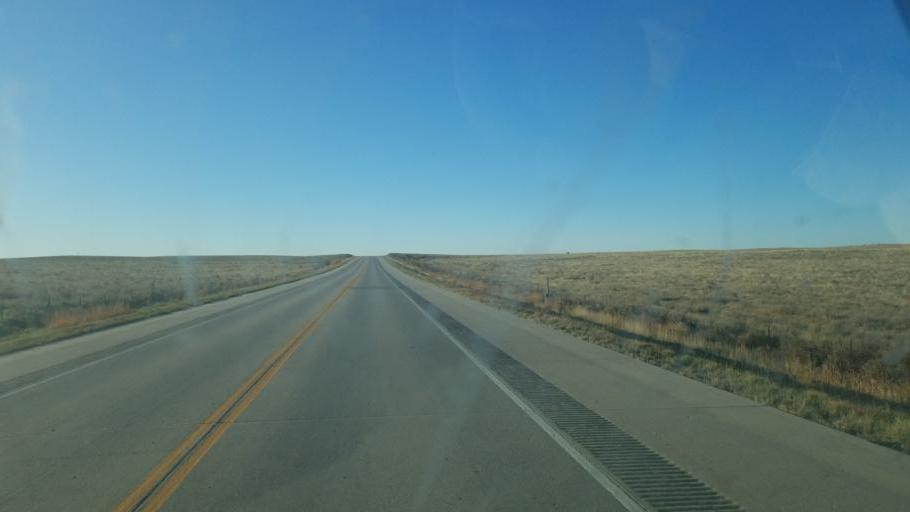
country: US
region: Colorado
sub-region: Kiowa County
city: Eads
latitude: 38.5444
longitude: -102.7859
